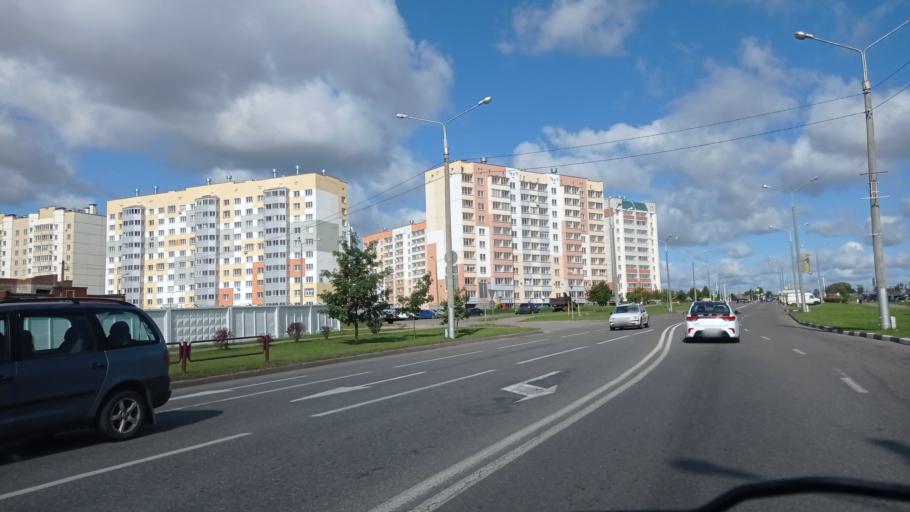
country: BY
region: Vitebsk
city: Vitebsk
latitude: 55.1708
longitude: 30.2574
